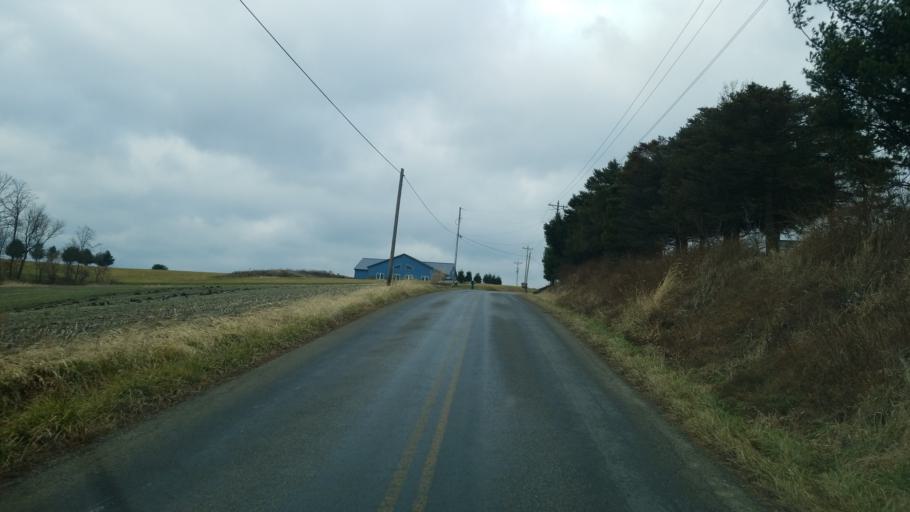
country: US
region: Ohio
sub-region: Holmes County
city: Millersburg
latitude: 40.5738
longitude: -81.9608
